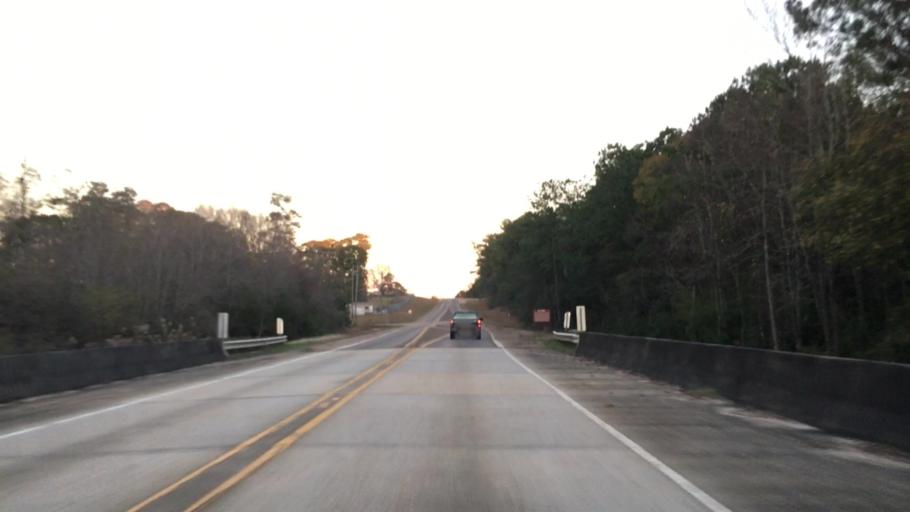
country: US
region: Louisiana
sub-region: Vernon Parish
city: Fort Polk South
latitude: 31.0294
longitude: -93.2145
